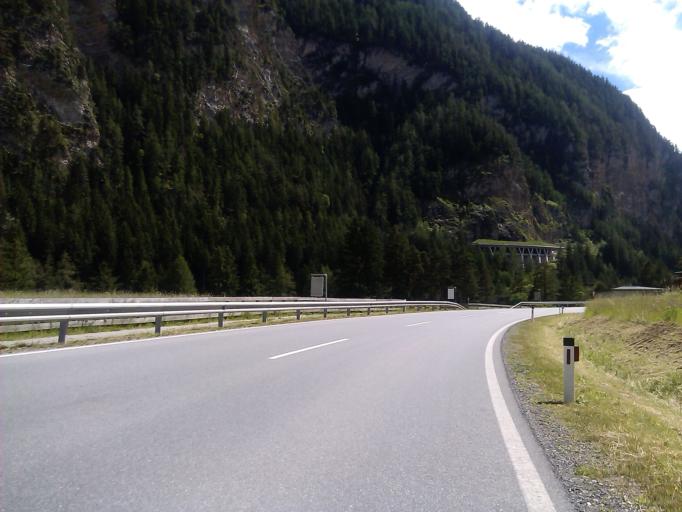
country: AT
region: Tyrol
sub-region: Politischer Bezirk Landeck
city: Pfunds
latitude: 46.9471
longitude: 10.5057
